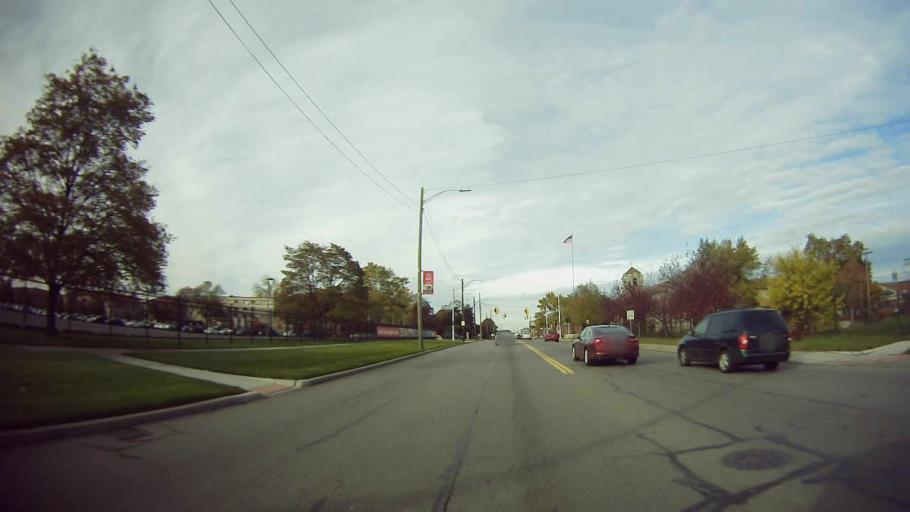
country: US
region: Michigan
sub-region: Wayne County
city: Highland Park
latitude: 42.4172
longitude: -83.1370
